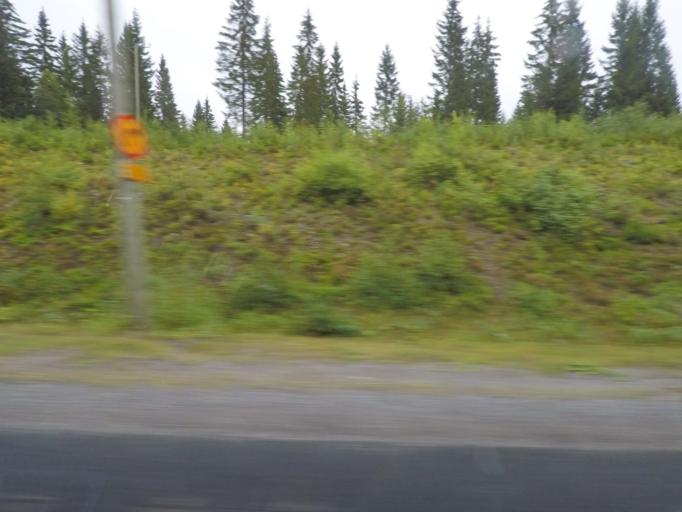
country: FI
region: Northern Savo
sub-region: Kuopio
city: Kuopio
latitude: 62.7301
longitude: 27.5857
